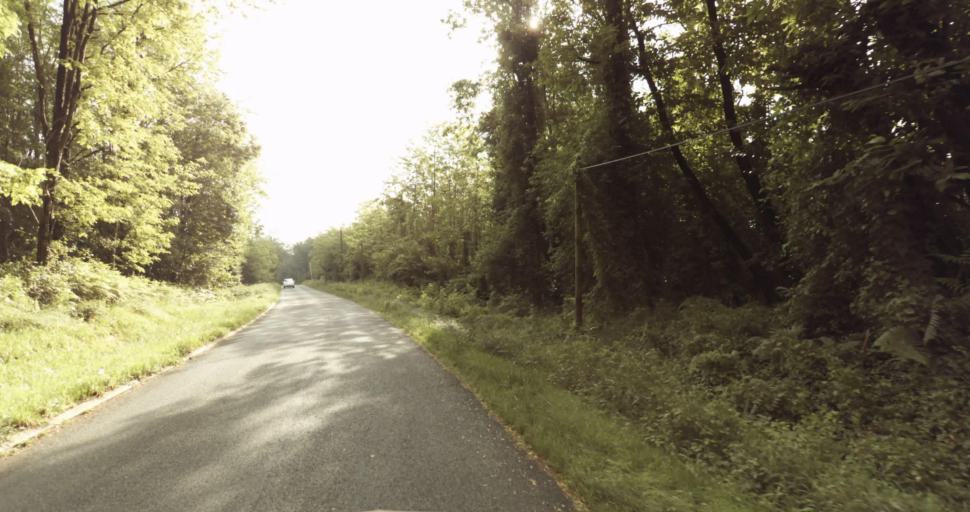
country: FR
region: Aquitaine
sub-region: Departement de la Dordogne
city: Lalinde
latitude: 44.9088
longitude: 0.7865
